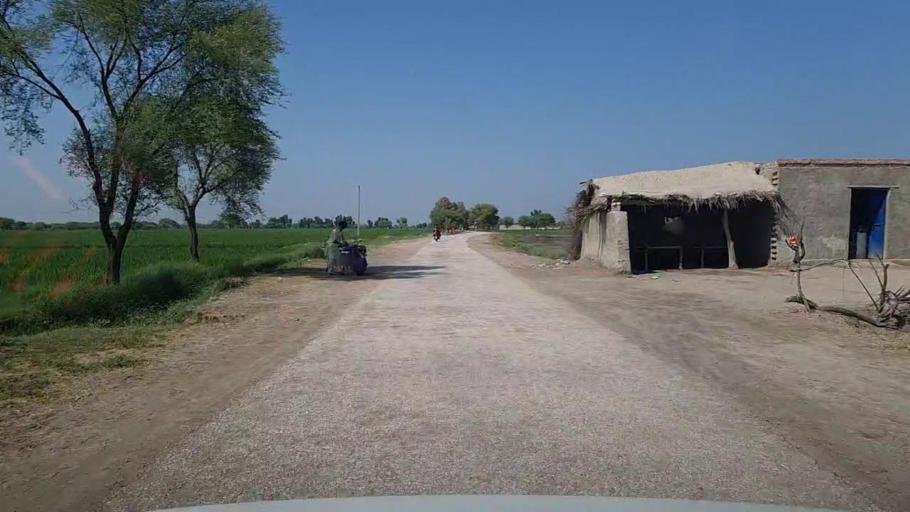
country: PK
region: Sindh
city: Kandhkot
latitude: 28.3249
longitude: 69.3667
